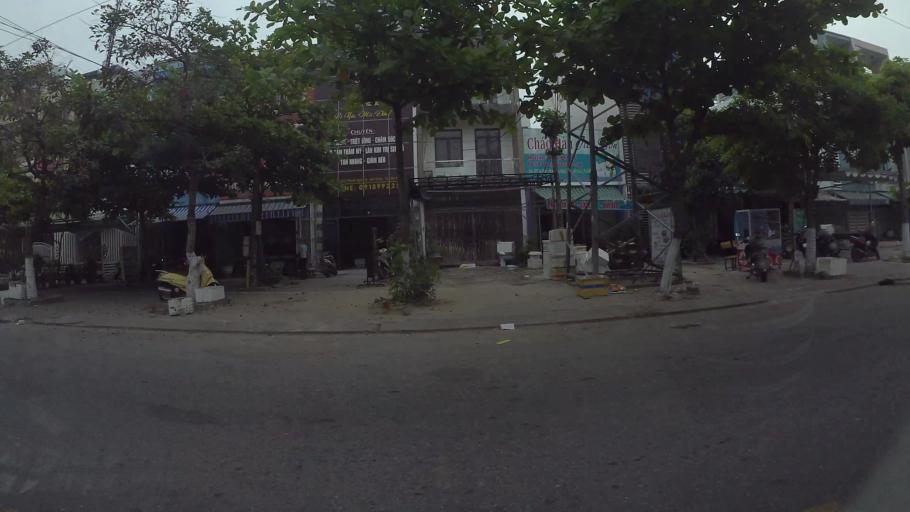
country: VN
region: Da Nang
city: Cam Le
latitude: 16.0336
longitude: 108.2185
